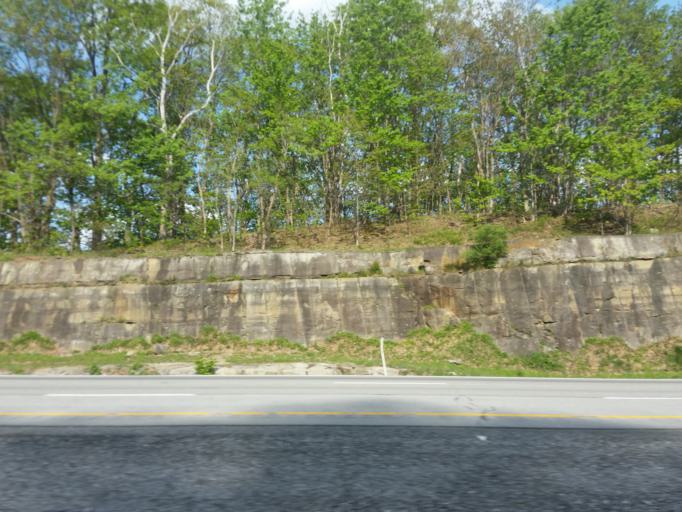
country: US
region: West Virginia
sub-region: Raleigh County
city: Shady Spring
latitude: 37.5672
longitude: -81.1127
